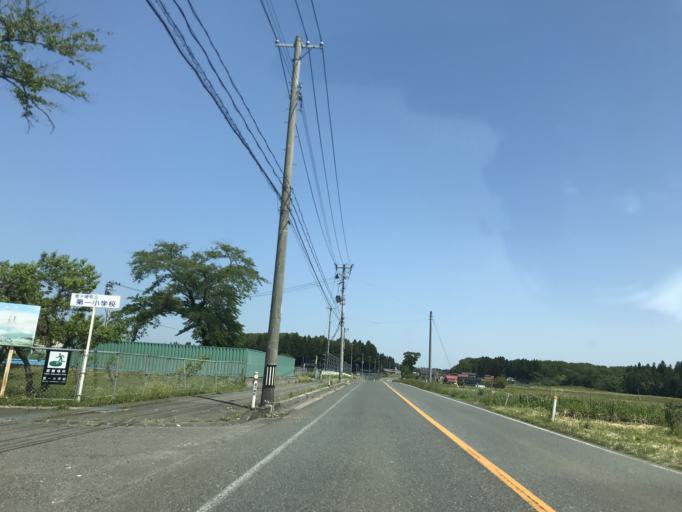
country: JP
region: Iwate
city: Kitakami
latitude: 39.2256
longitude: 141.0664
